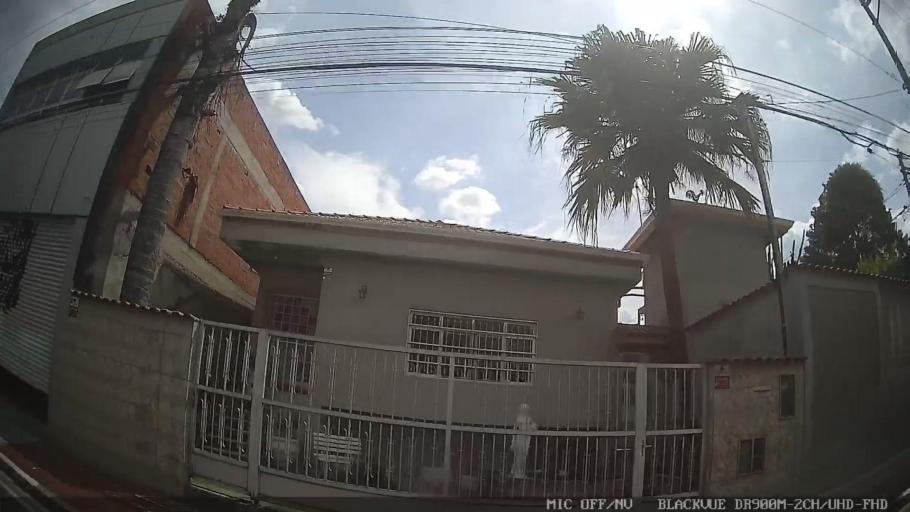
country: BR
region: Sao Paulo
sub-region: Poa
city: Poa
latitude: -23.5281
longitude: -46.3389
